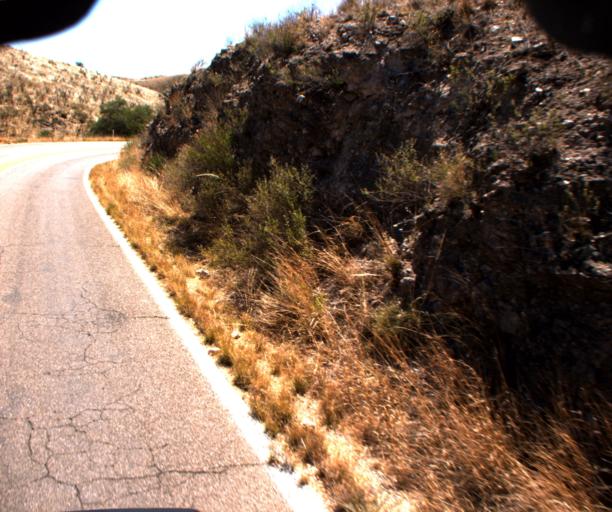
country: US
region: Arizona
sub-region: Santa Cruz County
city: Rio Rico
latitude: 31.3952
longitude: -111.0815
